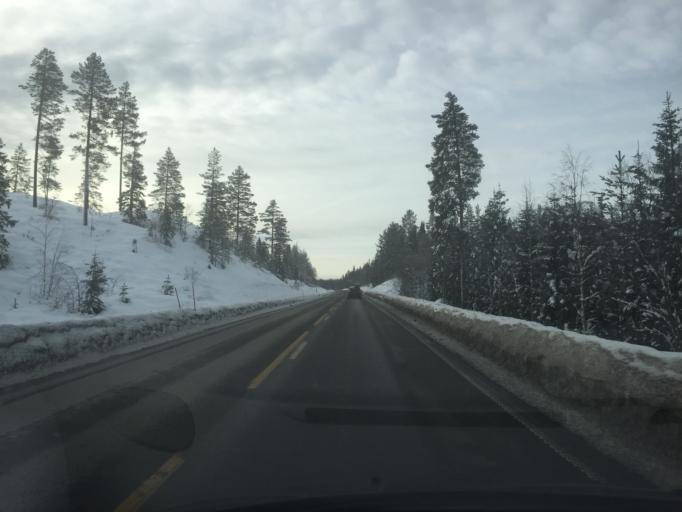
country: NO
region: Hedmark
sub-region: Trysil
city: Innbygda
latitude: 61.2592
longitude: 12.3056
